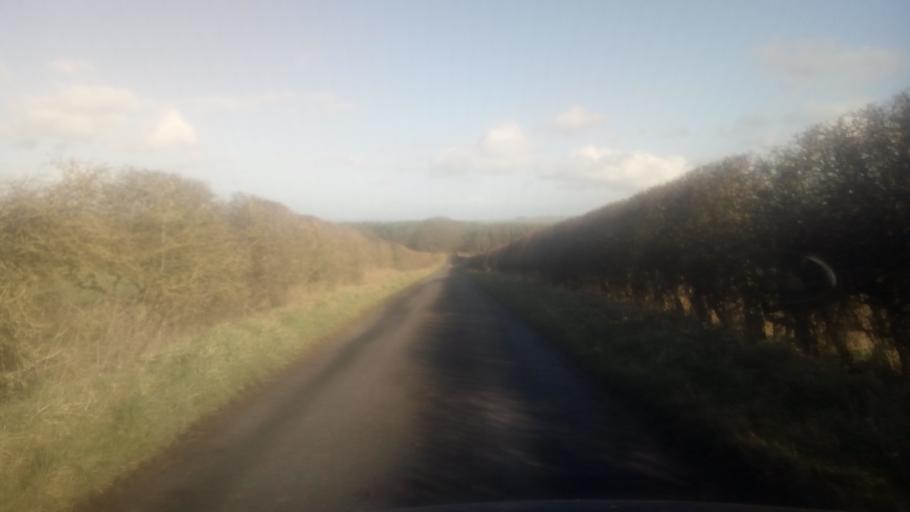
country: GB
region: Scotland
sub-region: The Scottish Borders
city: Jedburgh
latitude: 55.4942
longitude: -2.5168
